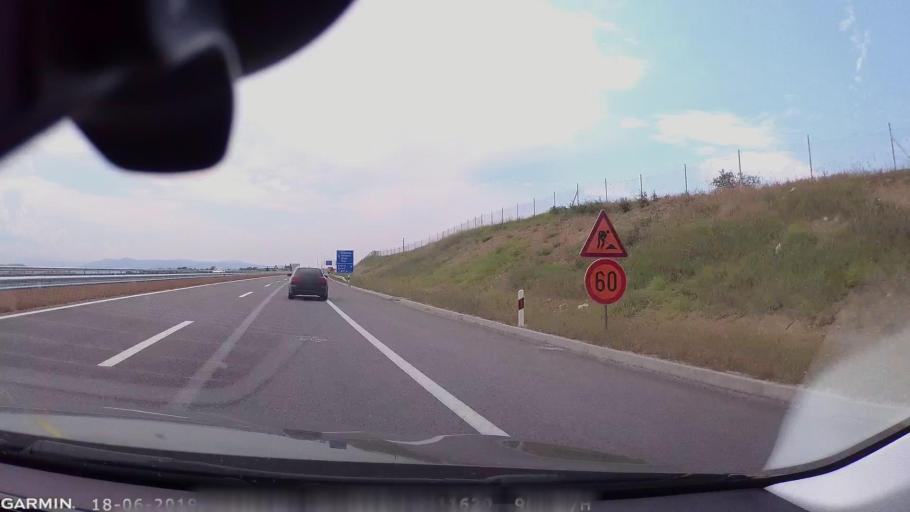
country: MK
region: Stip
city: Shtip
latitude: 41.7896
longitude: 22.1096
